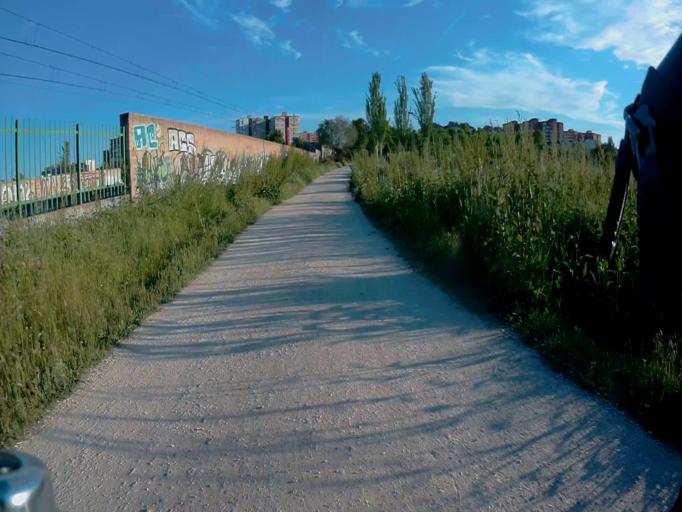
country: ES
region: Madrid
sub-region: Provincia de Madrid
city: Fuenlabrada
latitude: 40.2986
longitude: -3.7915
